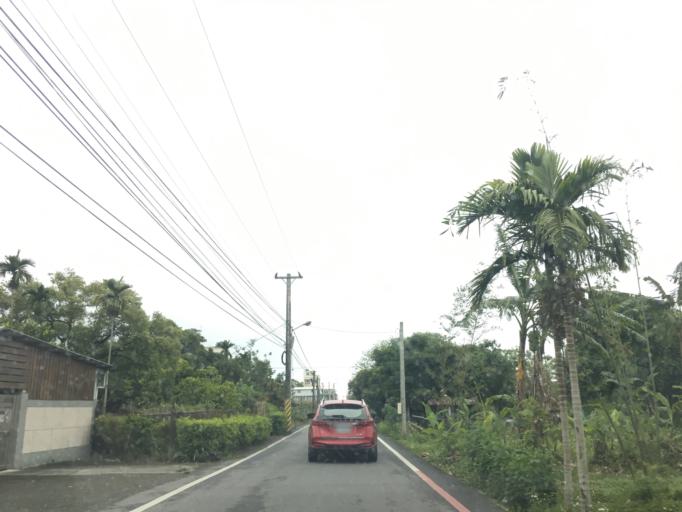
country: TW
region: Taiwan
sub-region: Hualien
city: Hualian
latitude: 23.9880
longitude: 121.5695
